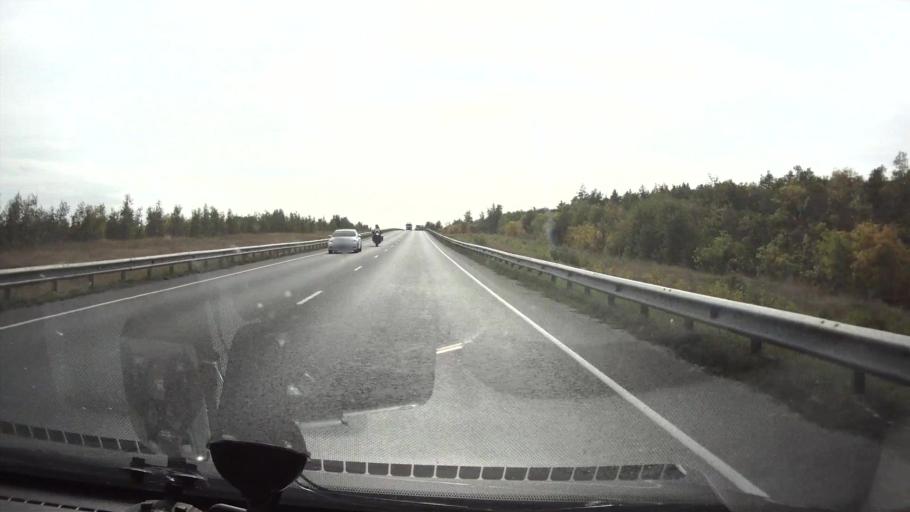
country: RU
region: Saratov
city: Balakovo
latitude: 52.1730
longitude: 47.8329
